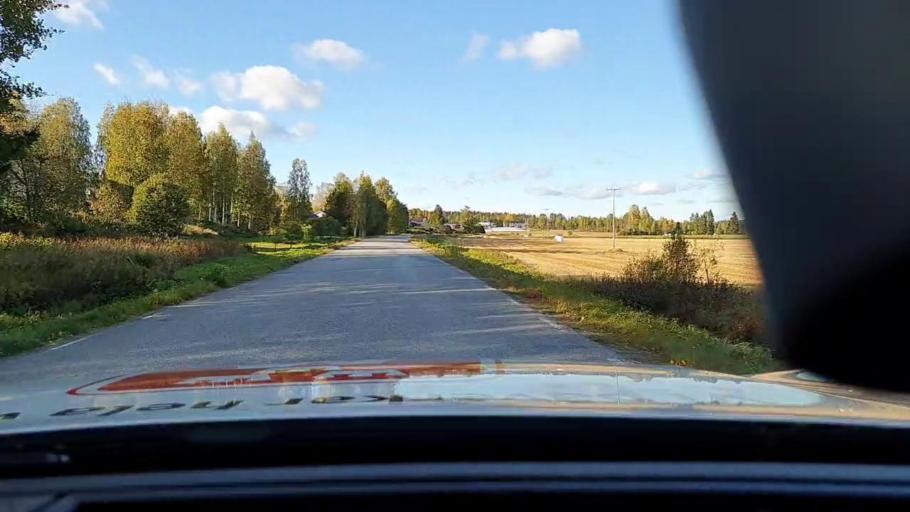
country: SE
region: Norrbotten
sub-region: Pitea Kommun
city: Norrfjarden
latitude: 65.5205
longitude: 21.4943
